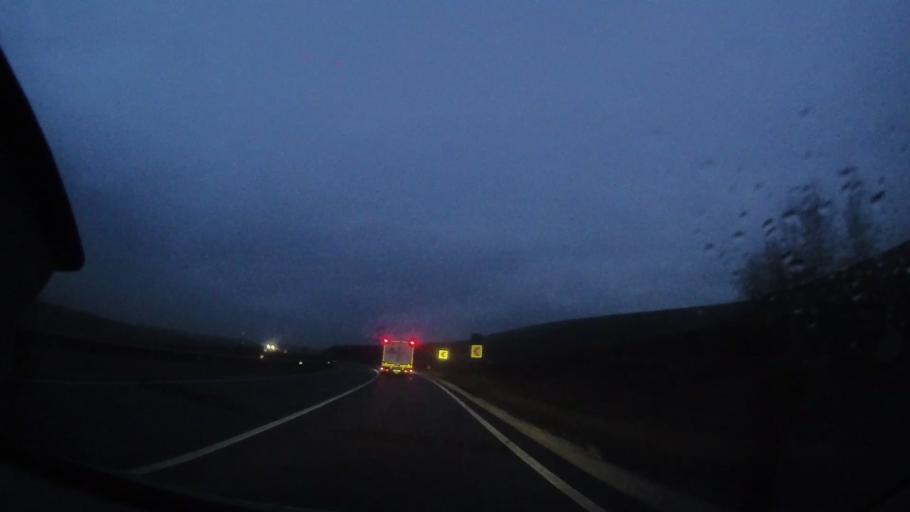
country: RO
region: Harghita
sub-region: Comuna Subcetate
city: Subcetate
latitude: 46.8486
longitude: 25.4686
